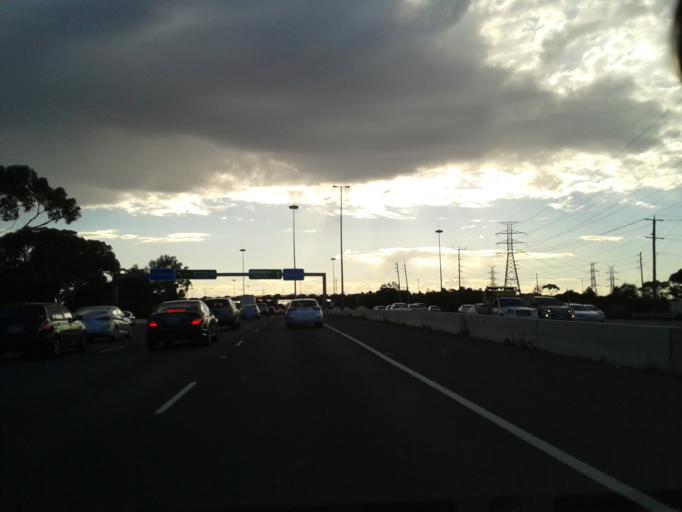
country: AU
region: Victoria
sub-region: Brimbank
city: Brooklyn
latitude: -37.8258
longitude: 144.8262
